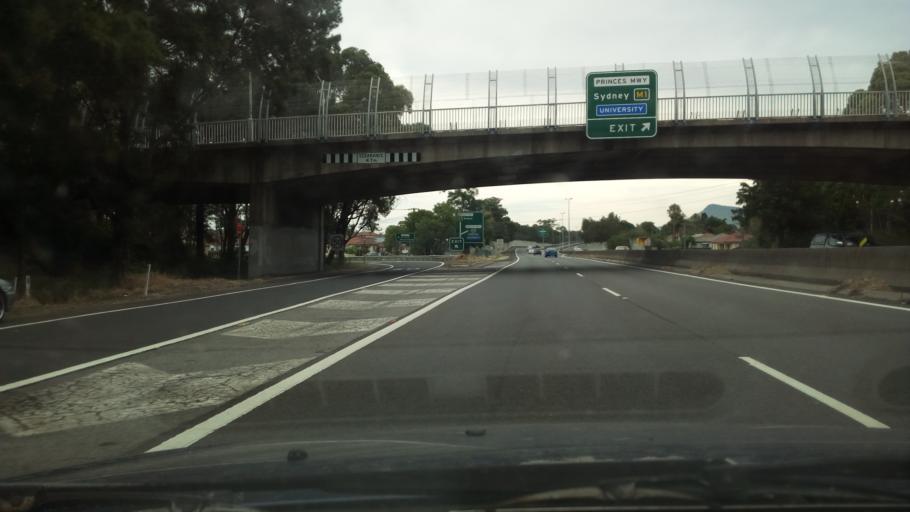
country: AU
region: New South Wales
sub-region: Wollongong
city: Gwynneville
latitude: -34.4112
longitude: 150.8872
